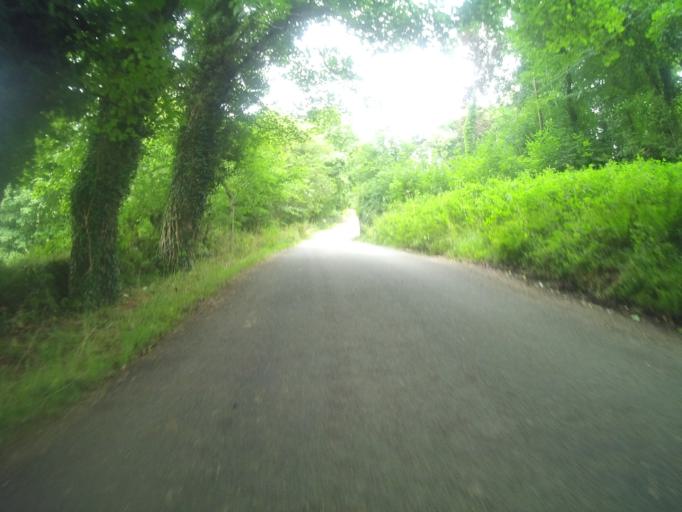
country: GB
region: England
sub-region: Devon
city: Buckfastleigh
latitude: 50.5413
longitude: -3.8892
